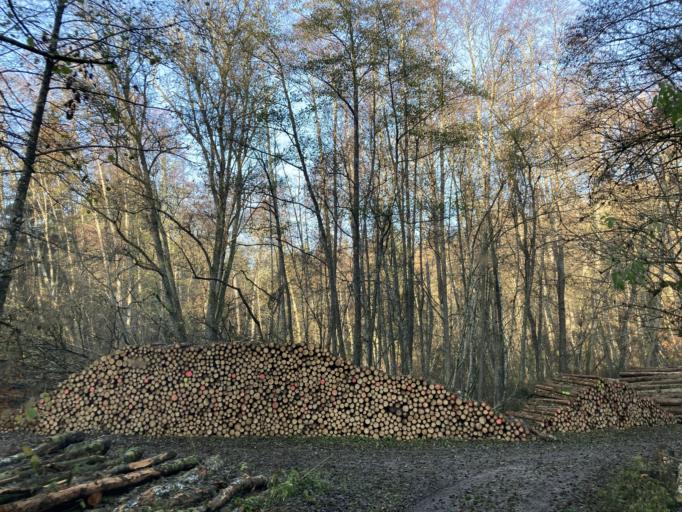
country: DE
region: Baden-Wuerttemberg
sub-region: Regierungsbezirk Stuttgart
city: Hildrizhausen
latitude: 48.5871
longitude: 8.9650
